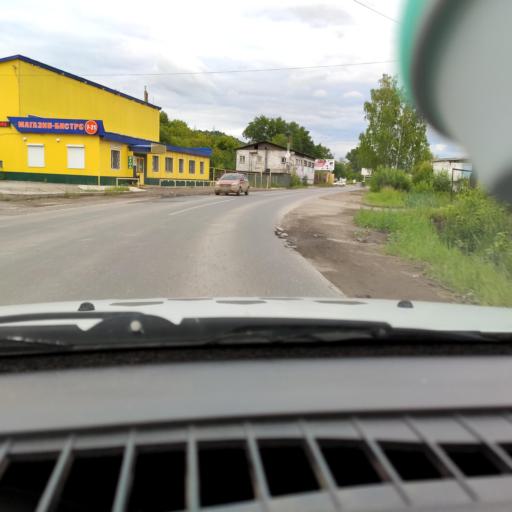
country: RU
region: Perm
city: Chusovoy
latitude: 58.3017
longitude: 57.8094
